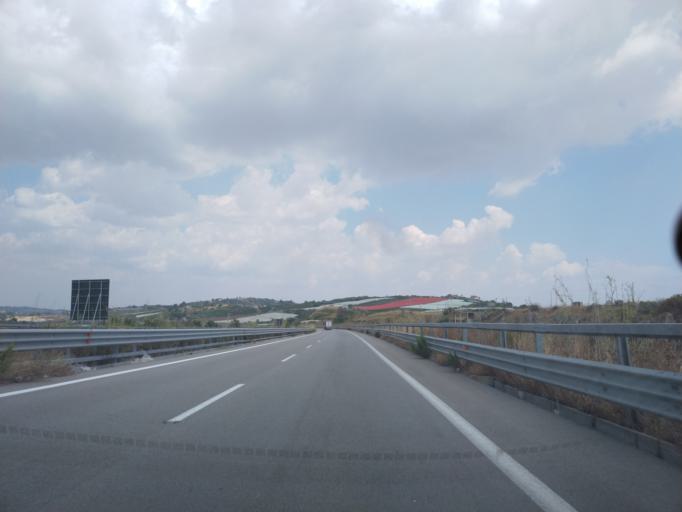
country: IT
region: Sicily
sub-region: Agrigento
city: Canicatti
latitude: 37.3834
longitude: 13.8187
